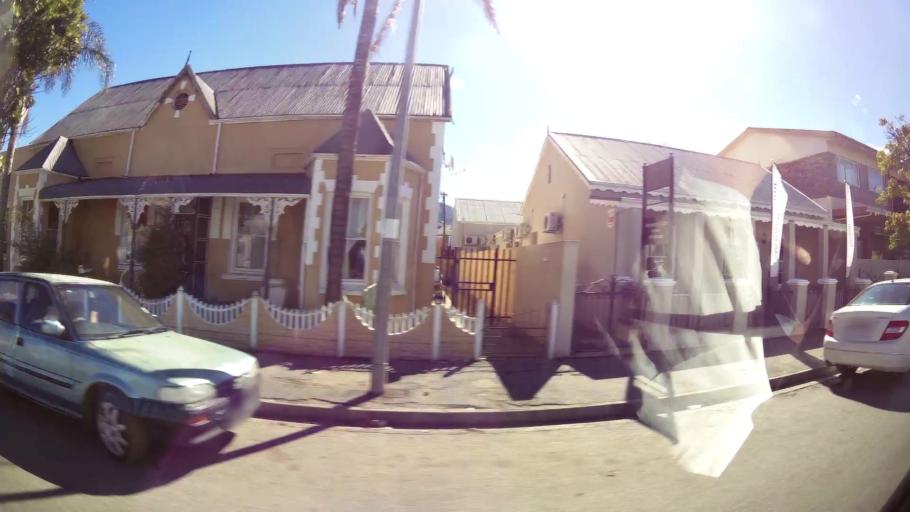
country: ZA
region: Western Cape
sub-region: Cape Winelands District Municipality
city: Ashton
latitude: -33.8046
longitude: 19.8801
